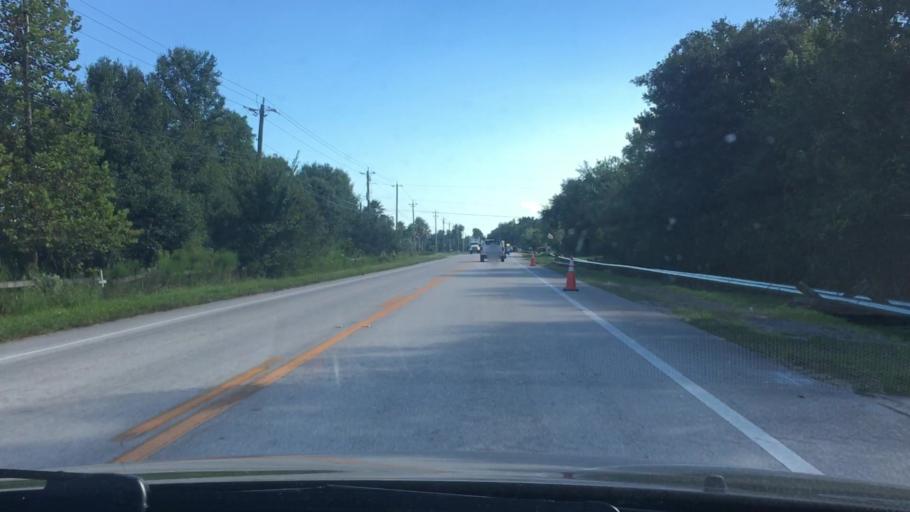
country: US
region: Florida
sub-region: Volusia County
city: Samsula-Spruce Creek
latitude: 29.0927
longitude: -81.0686
